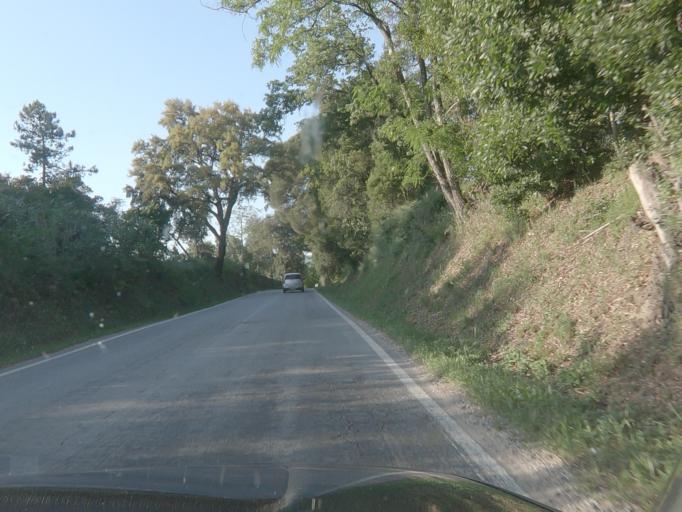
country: PT
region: Portalegre
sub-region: Portalegre
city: Portalegre
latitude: 39.3170
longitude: -7.4397
